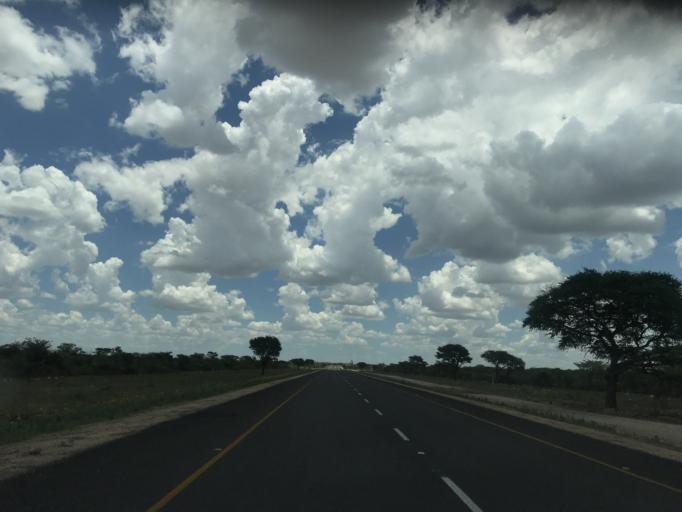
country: BW
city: Mabuli
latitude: -25.8031
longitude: 24.8351
